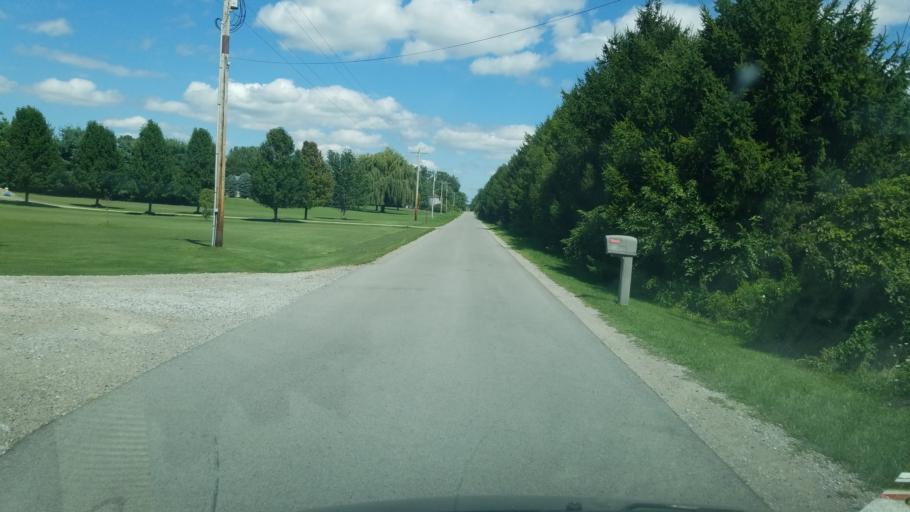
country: US
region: Ohio
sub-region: Henry County
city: Liberty Center
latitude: 41.4602
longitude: -83.9411
